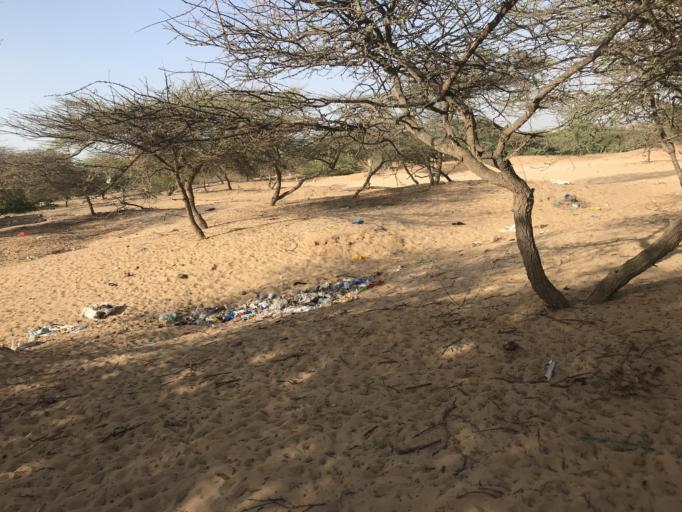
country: SN
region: Saint-Louis
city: Saint-Louis
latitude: 16.0358
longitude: -16.4415
